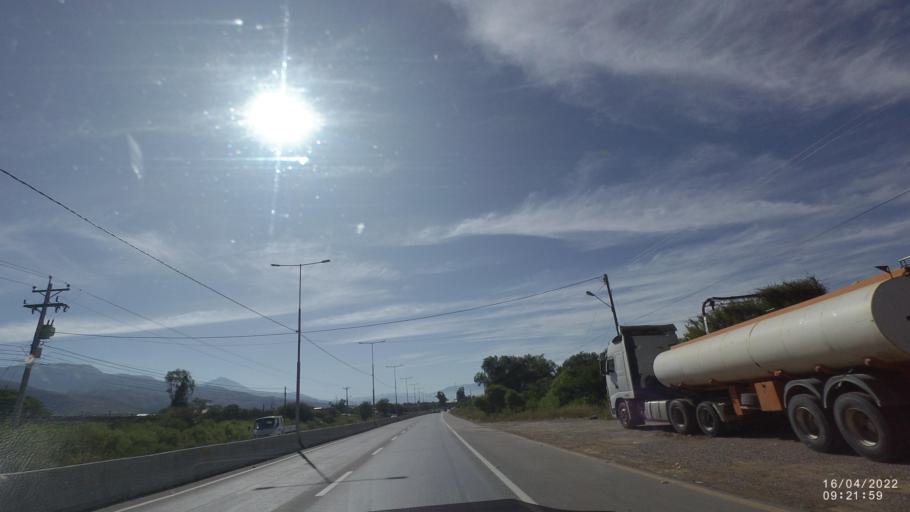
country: BO
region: Cochabamba
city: Cliza
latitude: -17.5329
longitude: -65.9757
